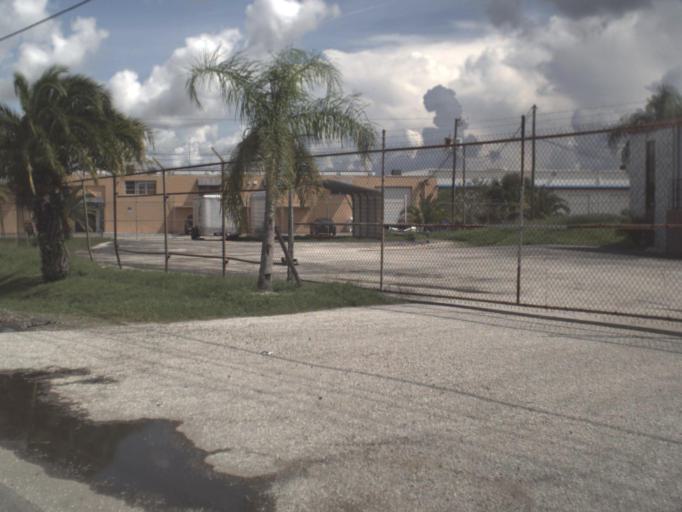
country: US
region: Florida
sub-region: Hillsborough County
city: Egypt Lake-Leto
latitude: 28.0057
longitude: -82.5294
